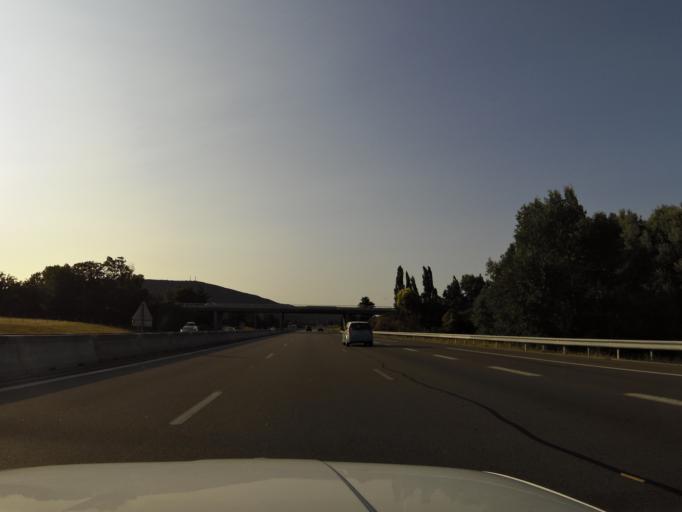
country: FR
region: Rhone-Alpes
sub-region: Departement de la Drome
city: Saint-Marcel-les-Sauzet
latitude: 44.5932
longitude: 4.7991
